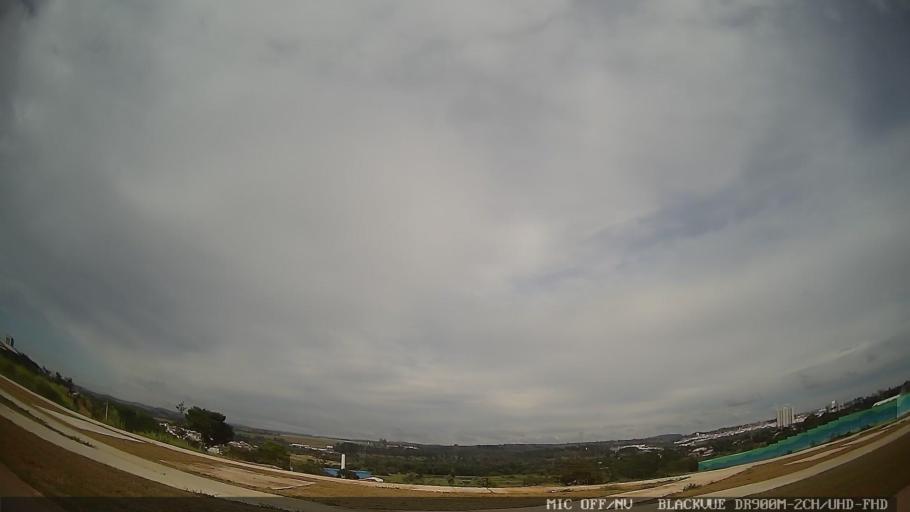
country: BR
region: Sao Paulo
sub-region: Salto
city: Salto
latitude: -23.1813
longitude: -47.2695
